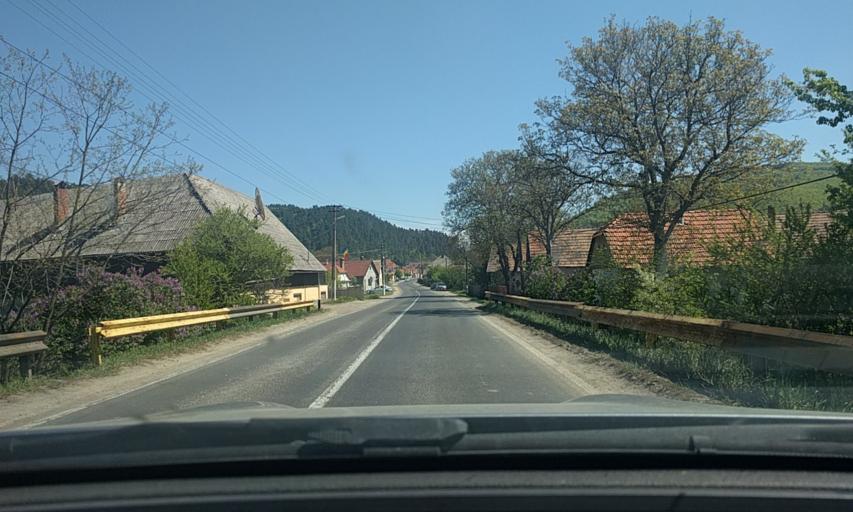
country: RO
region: Brasov
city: Tunelu-Teliu
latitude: 45.7032
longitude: 25.8466
